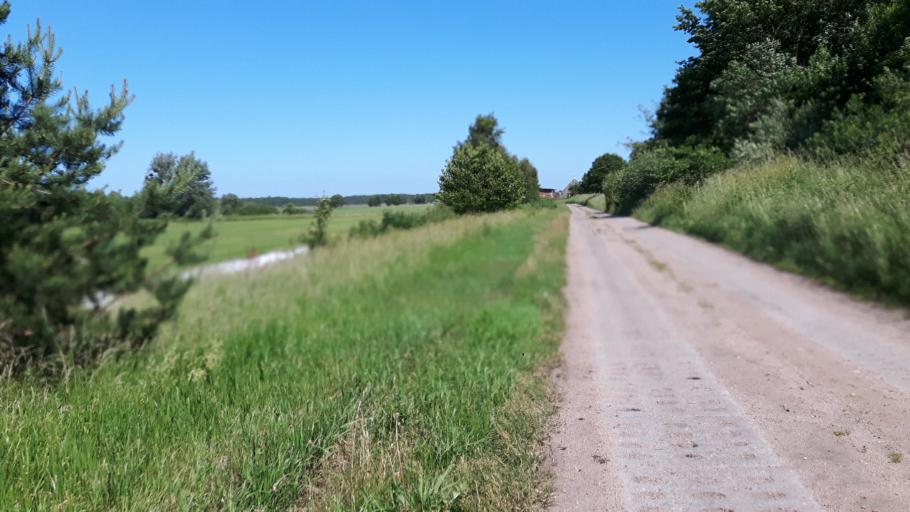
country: PL
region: Pomeranian Voivodeship
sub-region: Powiat slupski
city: Glowczyce
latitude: 54.6418
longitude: 17.3630
